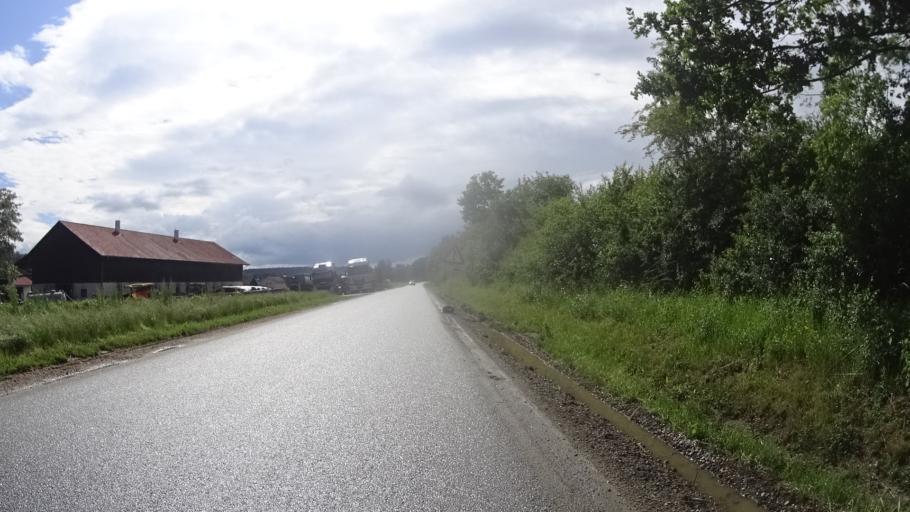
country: DE
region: Bavaria
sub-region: Lower Bavaria
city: Schalkham
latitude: 48.4452
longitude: 12.4387
